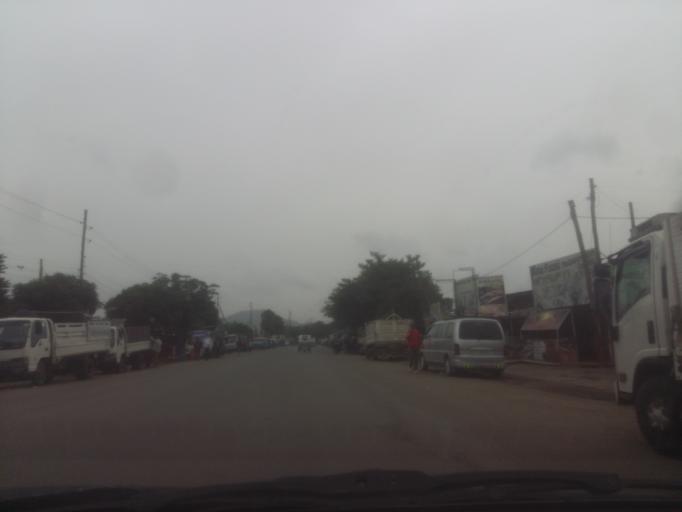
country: ET
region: Oromiya
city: Bishoftu
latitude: 8.7935
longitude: 38.9017
